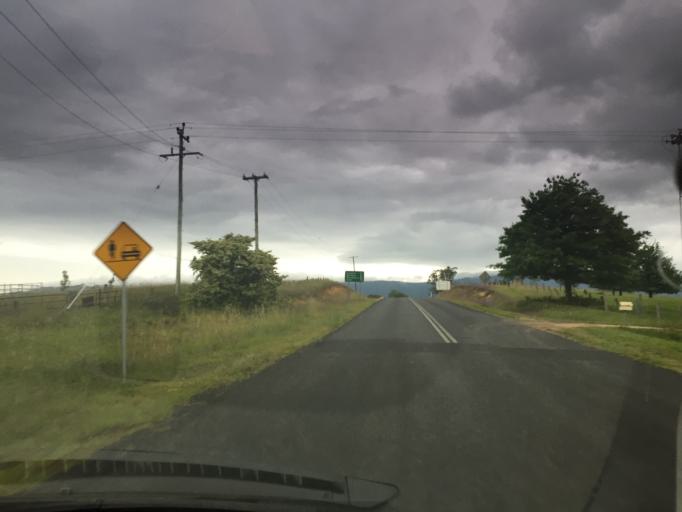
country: AU
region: New South Wales
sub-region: Bega Valley
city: Bega
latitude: -36.6450
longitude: 149.5865
